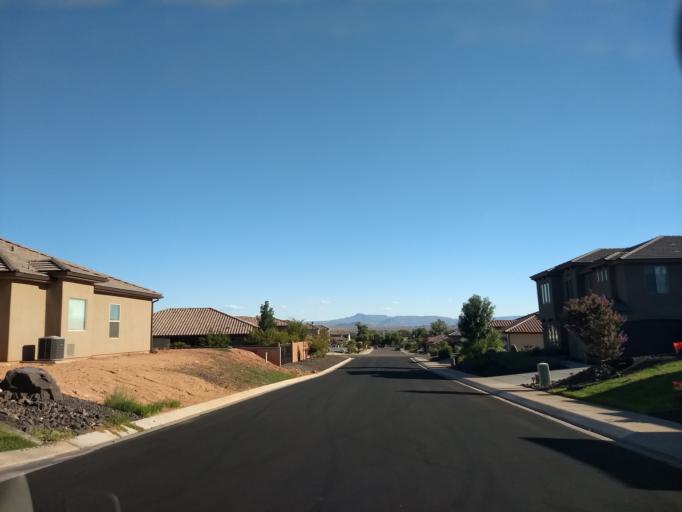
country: US
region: Utah
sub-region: Washington County
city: Washington
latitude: 37.1228
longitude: -113.5076
